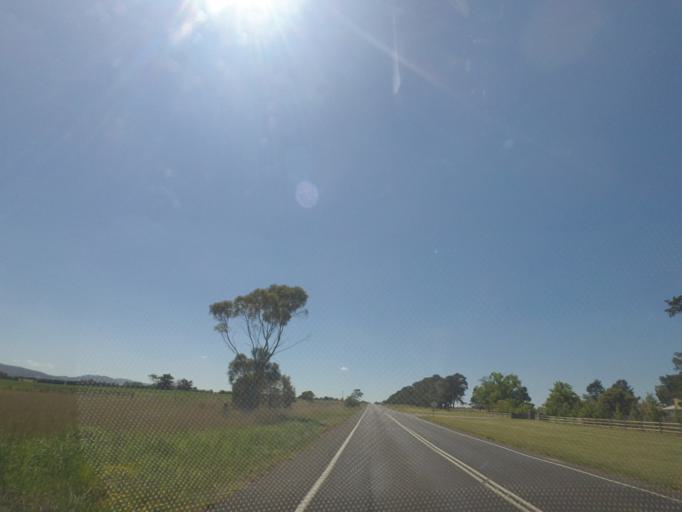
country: AU
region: Victoria
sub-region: Hume
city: Sunbury
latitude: -37.4612
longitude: 144.7414
